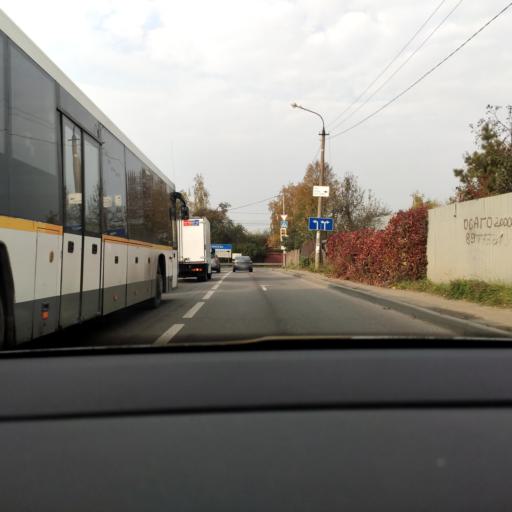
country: RU
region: Moskovskaya
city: Lesnyye Polyany
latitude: 55.9872
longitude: 37.8694
